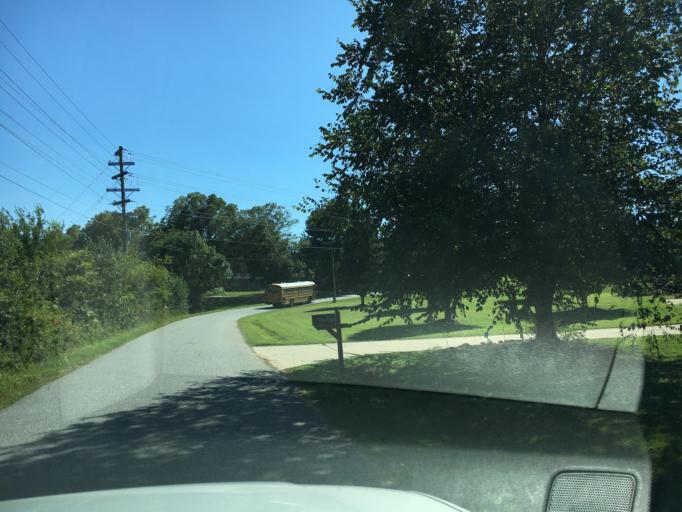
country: US
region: South Carolina
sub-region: Spartanburg County
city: Duncan
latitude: 34.8646
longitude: -82.1696
